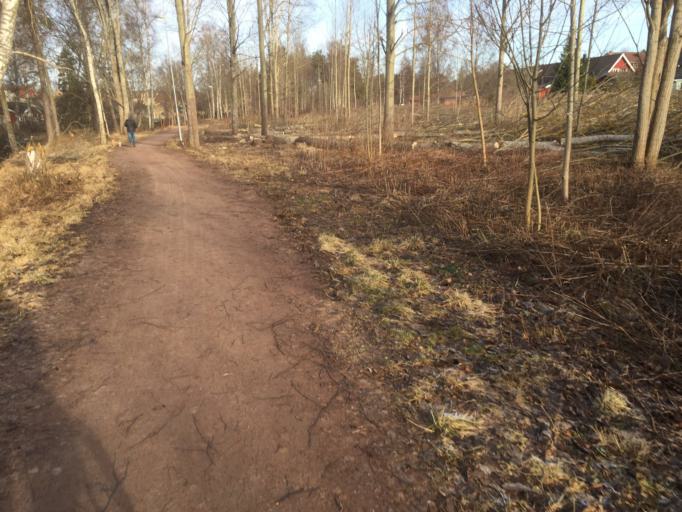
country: SE
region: Joenkoeping
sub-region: Aneby Kommun
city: Aneby
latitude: 57.8328
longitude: 14.8117
